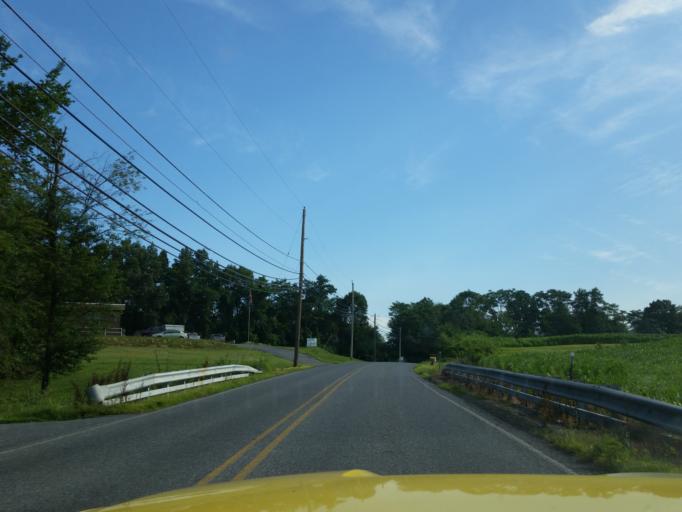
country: US
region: Pennsylvania
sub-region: Lebanon County
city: Jonestown
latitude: 40.4186
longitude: -76.4693
